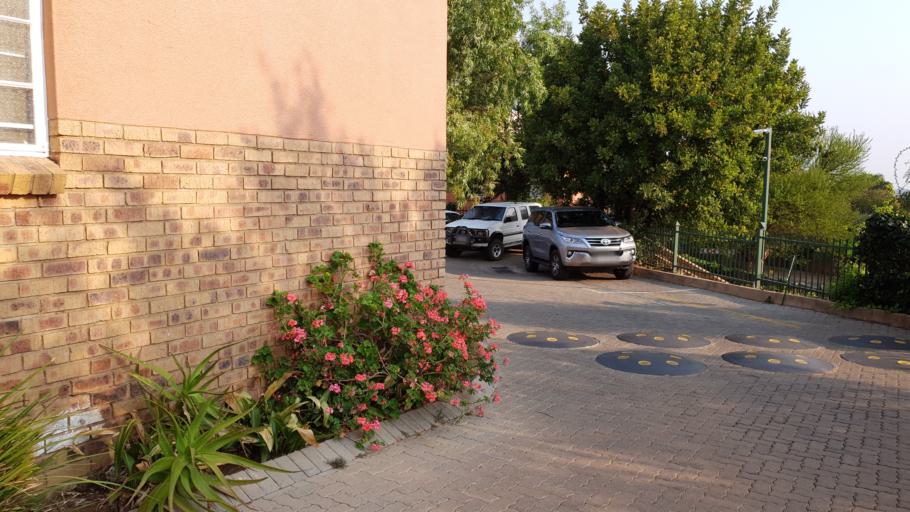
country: ZA
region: Gauteng
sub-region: City of Tshwane Metropolitan Municipality
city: Centurion
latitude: -25.8303
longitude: 28.2524
